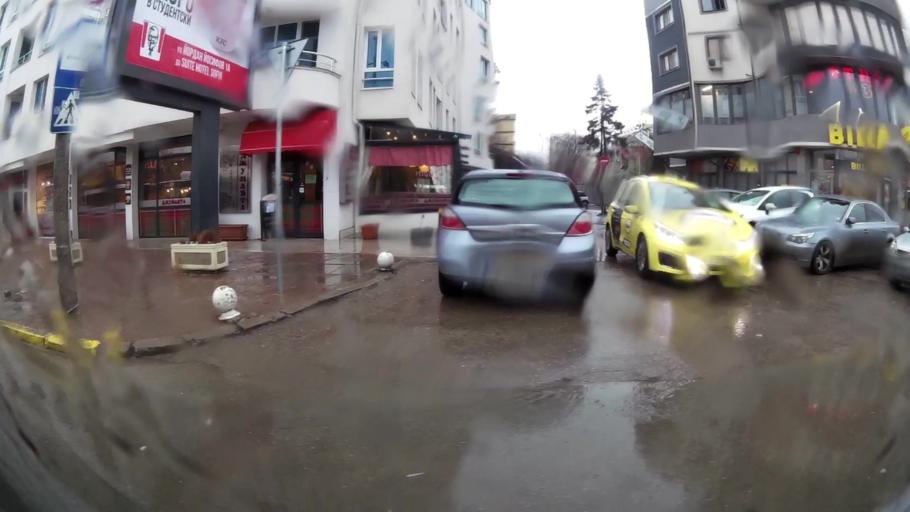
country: BG
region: Sofia-Capital
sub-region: Stolichna Obshtina
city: Sofia
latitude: 42.6537
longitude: 23.3441
